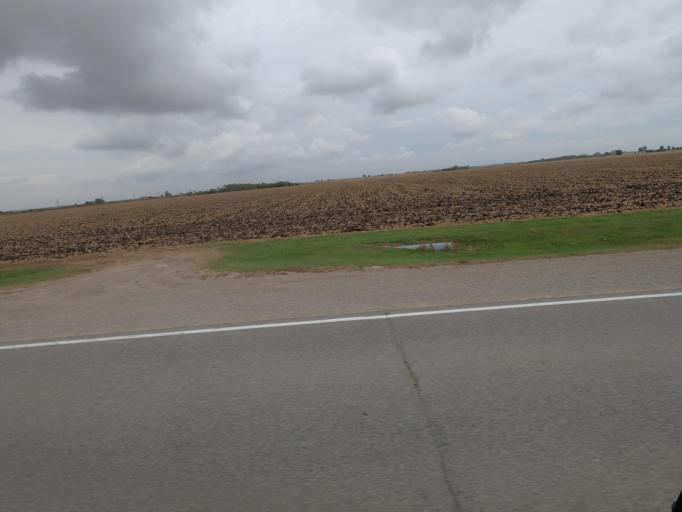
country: US
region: Iowa
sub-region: Wapello County
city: Ottumwa
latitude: 40.9867
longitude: -92.2368
